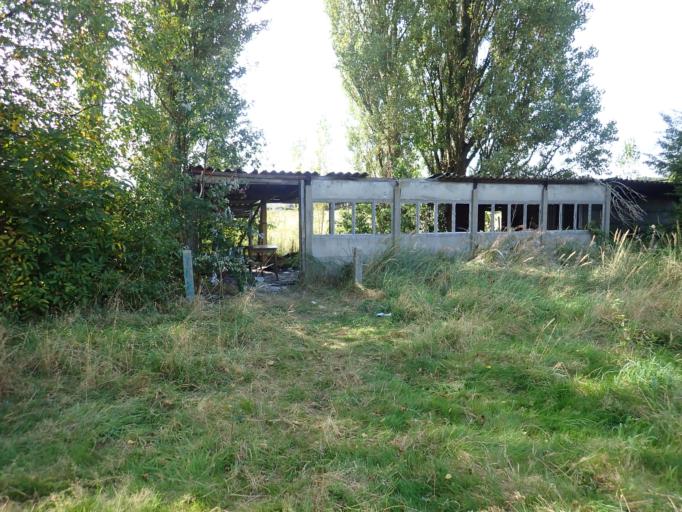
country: BE
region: Flanders
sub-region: Provincie Antwerpen
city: Lint
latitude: 51.1277
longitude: 4.5046
